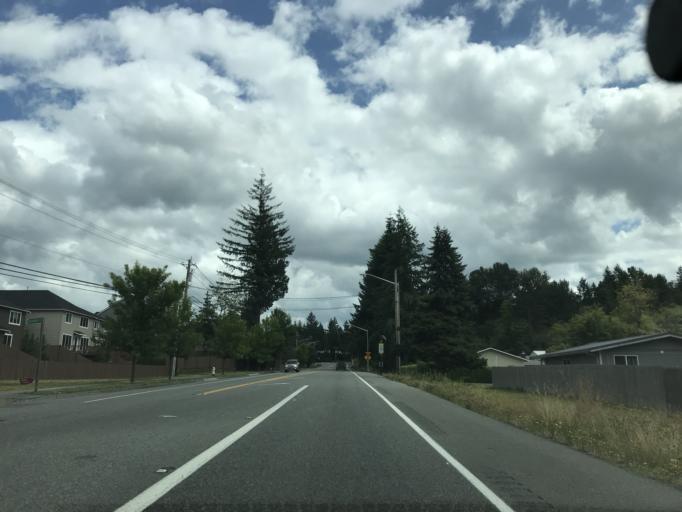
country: US
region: Washington
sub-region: King County
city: Maple Heights-Lake Desire
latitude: 47.4395
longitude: -122.1247
